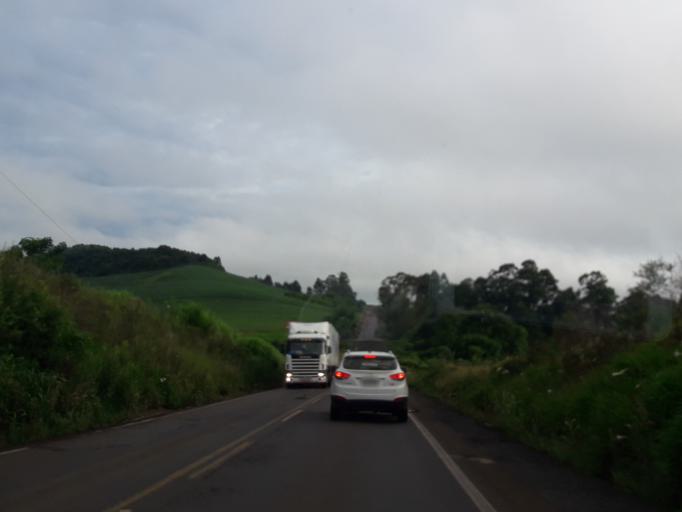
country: AR
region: Misiones
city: Bernardo de Irigoyen
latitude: -26.3368
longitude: -53.5462
